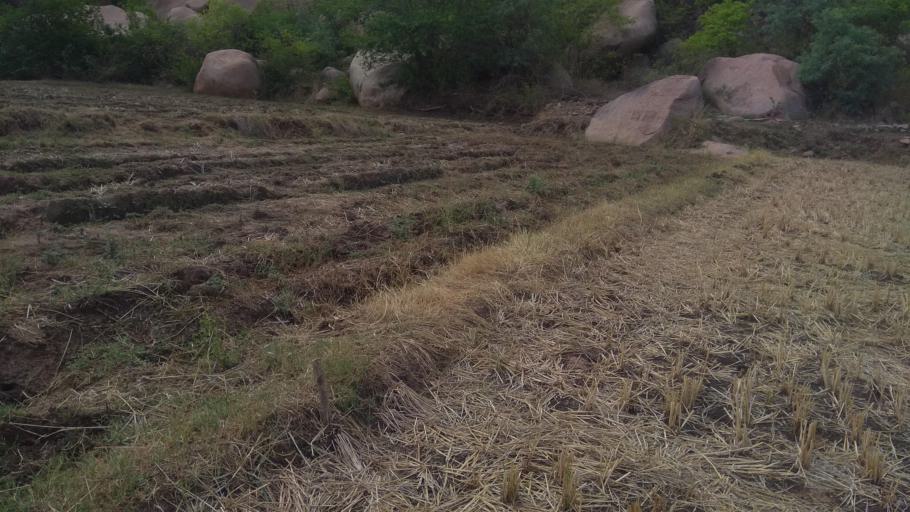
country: IN
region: Telangana
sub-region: Mahbubnagar
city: Farrukhnagar
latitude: 16.8912
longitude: 78.4922
